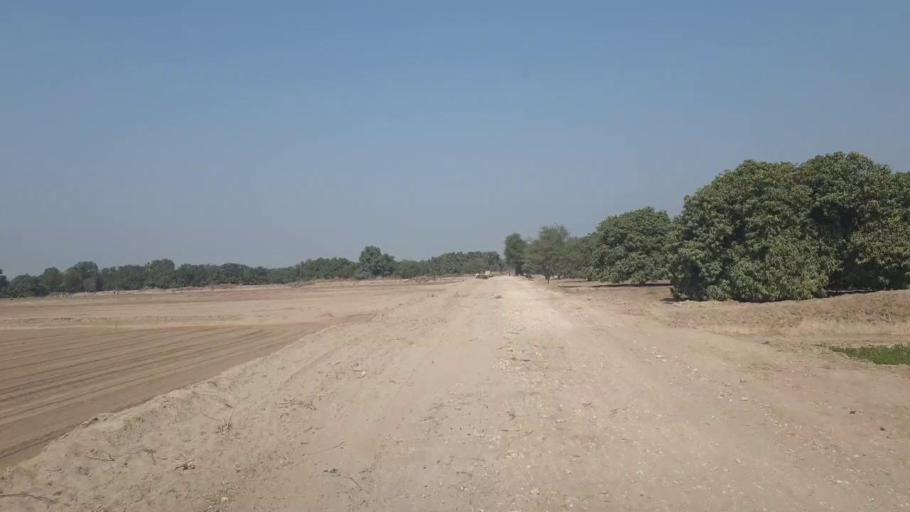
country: PK
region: Sindh
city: Tando Allahyar
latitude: 25.4492
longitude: 68.8326
